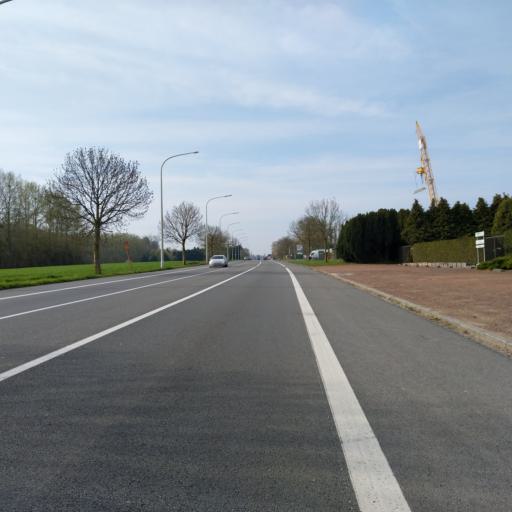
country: BE
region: Wallonia
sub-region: Province du Hainaut
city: Frameries
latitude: 50.4100
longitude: 3.9236
